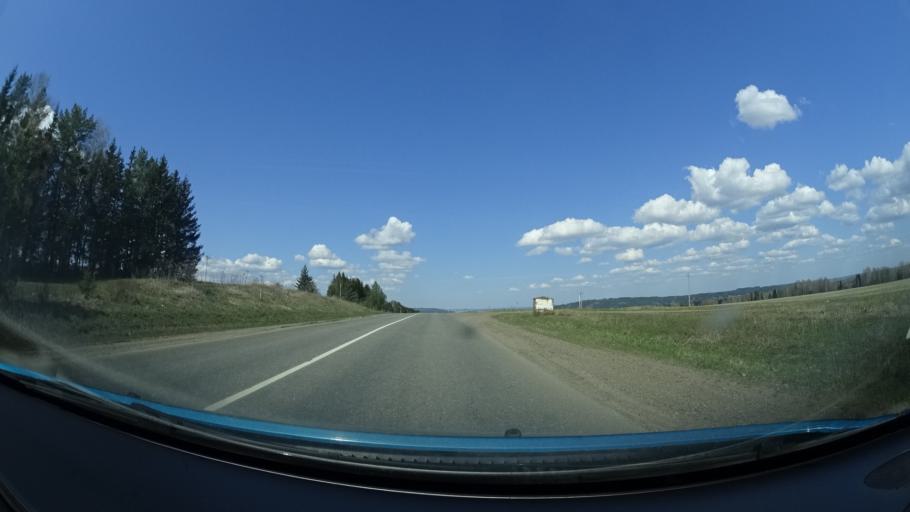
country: RU
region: Perm
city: Osa
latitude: 57.2671
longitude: 55.5729
